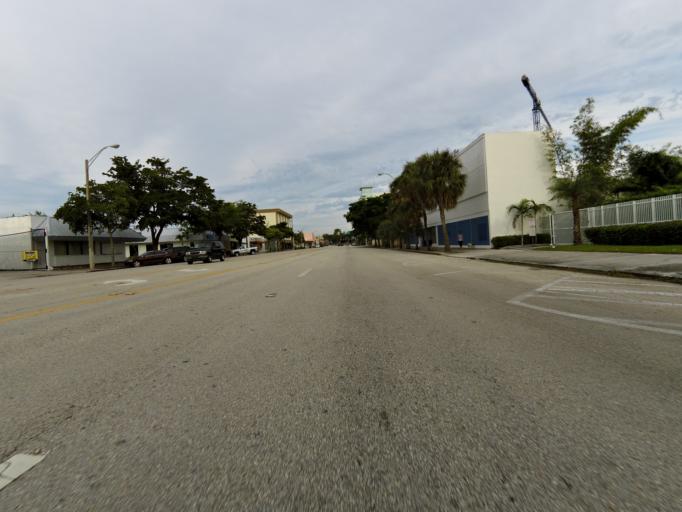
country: US
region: Florida
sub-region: Broward County
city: Hollywood
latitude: 26.0112
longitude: -80.1525
